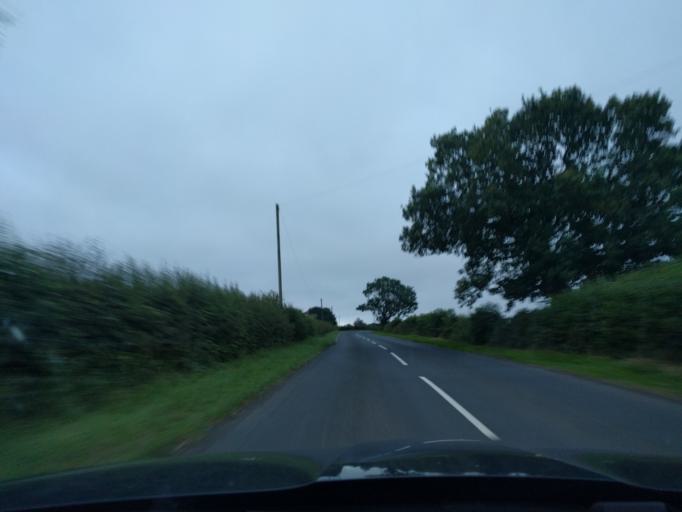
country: GB
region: England
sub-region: Northumberland
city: Acklington
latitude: 55.2512
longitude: -1.6543
